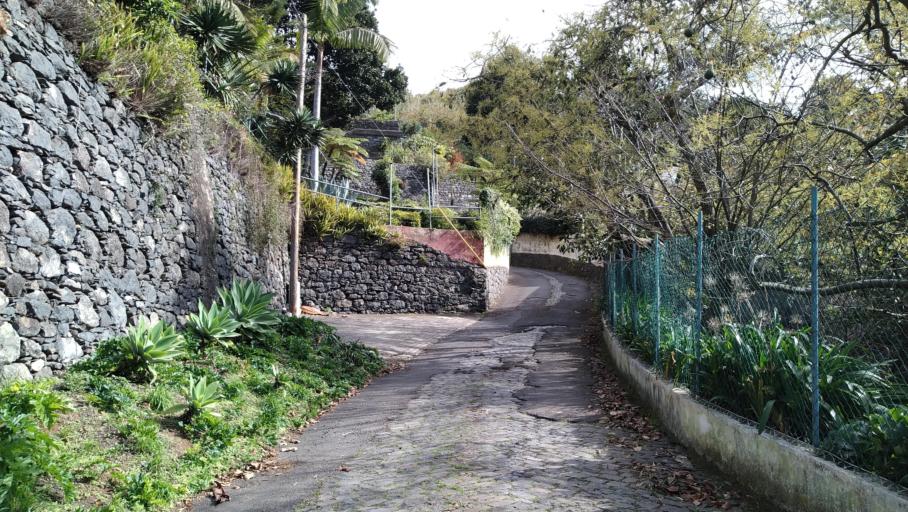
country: PT
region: Madeira
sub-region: Funchal
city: Nossa Senhora do Monte
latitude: 32.6598
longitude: -16.8775
